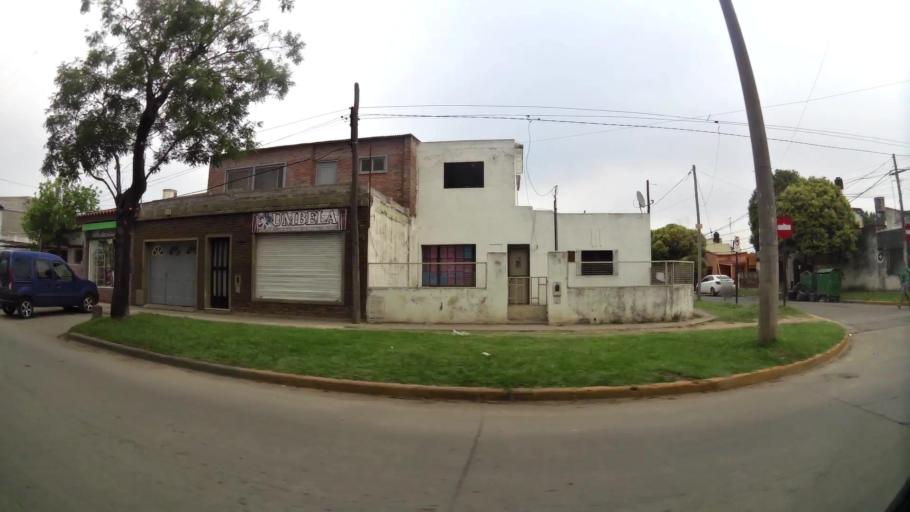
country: AR
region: Santa Fe
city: Granadero Baigorria
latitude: -32.8937
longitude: -60.7087
